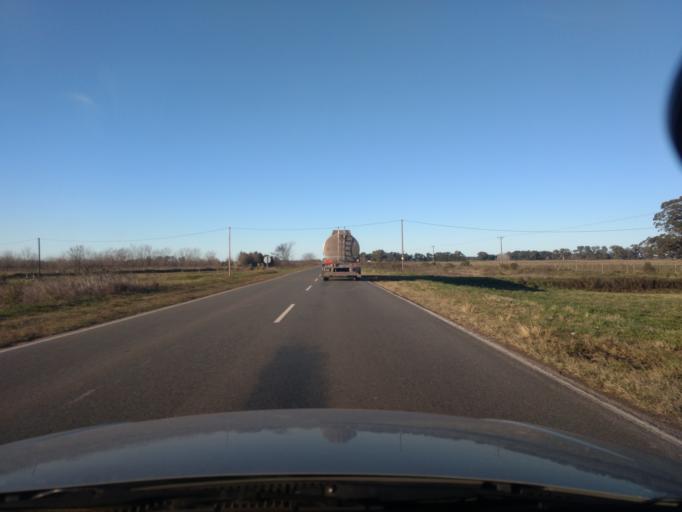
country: AR
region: Buenos Aires
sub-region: Partido de Lujan
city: Lujan
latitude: -34.6414
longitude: -59.1060
